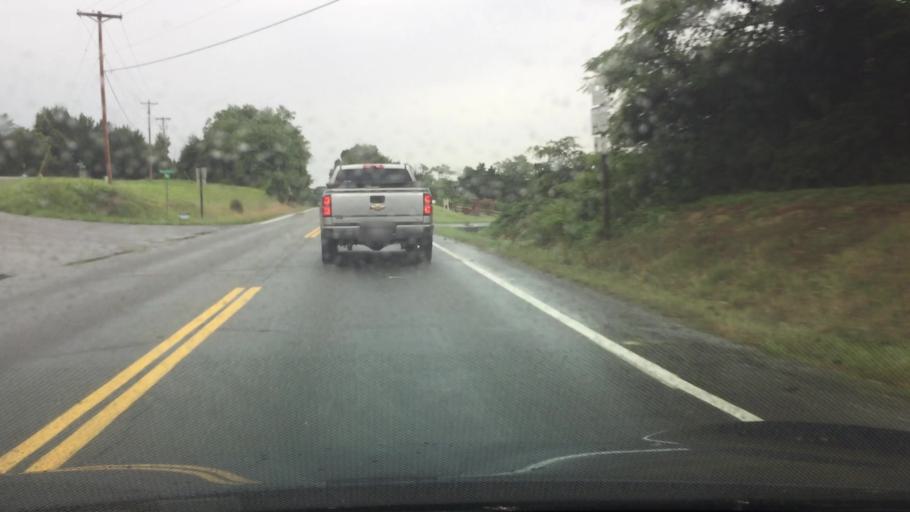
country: US
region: Virginia
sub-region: Bedford County
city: Forest
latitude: 37.3734
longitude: -79.3812
